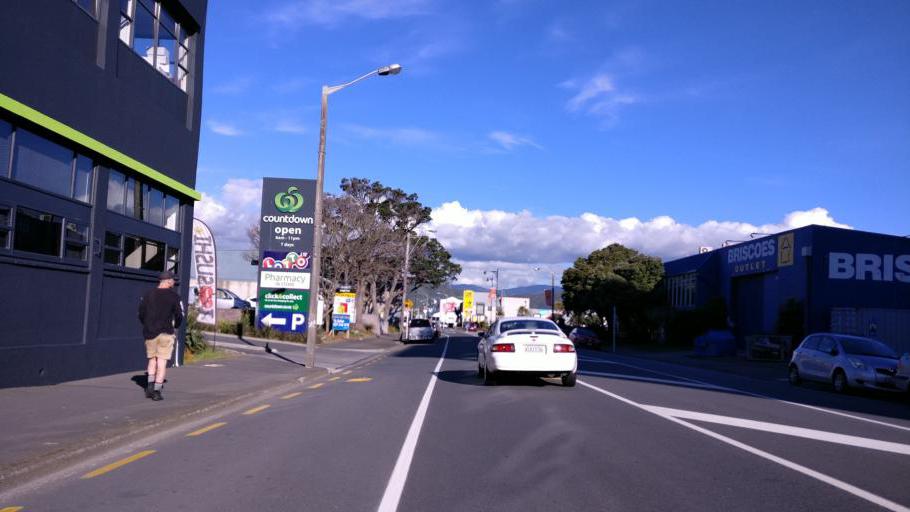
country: NZ
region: Wellington
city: Petone
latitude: -41.2232
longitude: 174.8713
